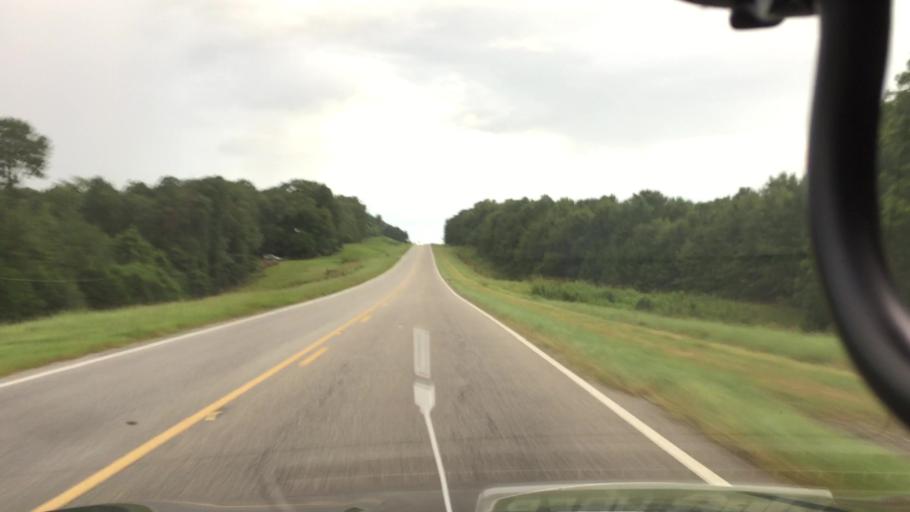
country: US
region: Alabama
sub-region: Pike County
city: Troy
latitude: 31.7187
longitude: -85.9600
